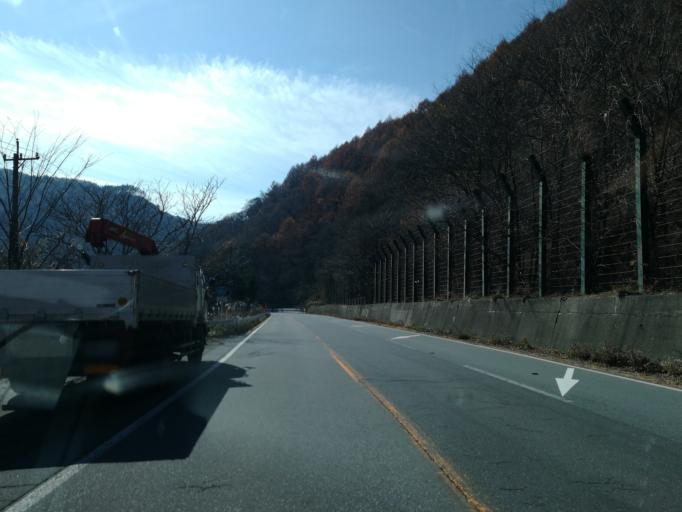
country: JP
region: Nagano
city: Ueda
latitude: 36.4925
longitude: 138.3612
